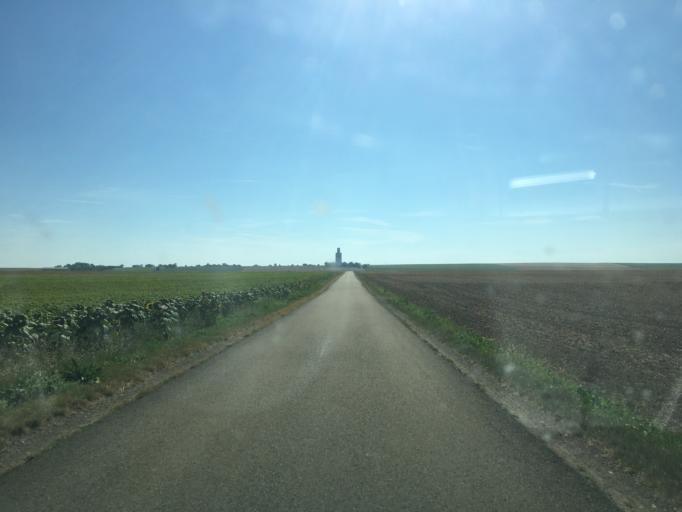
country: FR
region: Bourgogne
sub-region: Departement de l'Yonne
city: Joigny
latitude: 47.9186
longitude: 3.4086
